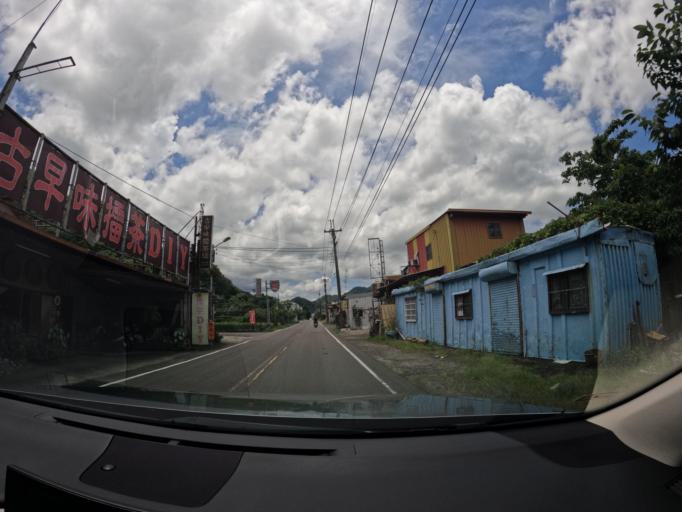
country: TW
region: Taiwan
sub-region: Miaoli
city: Miaoli
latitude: 24.6090
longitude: 121.0035
